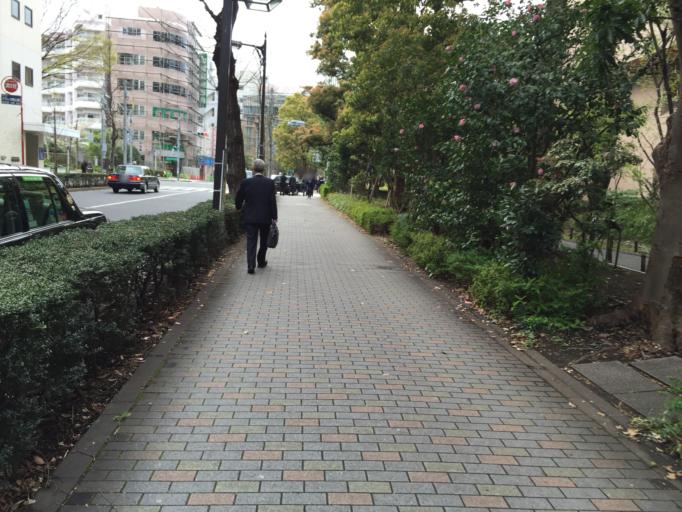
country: JP
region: Tokyo
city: Tokyo
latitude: 35.6670
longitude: 139.7767
